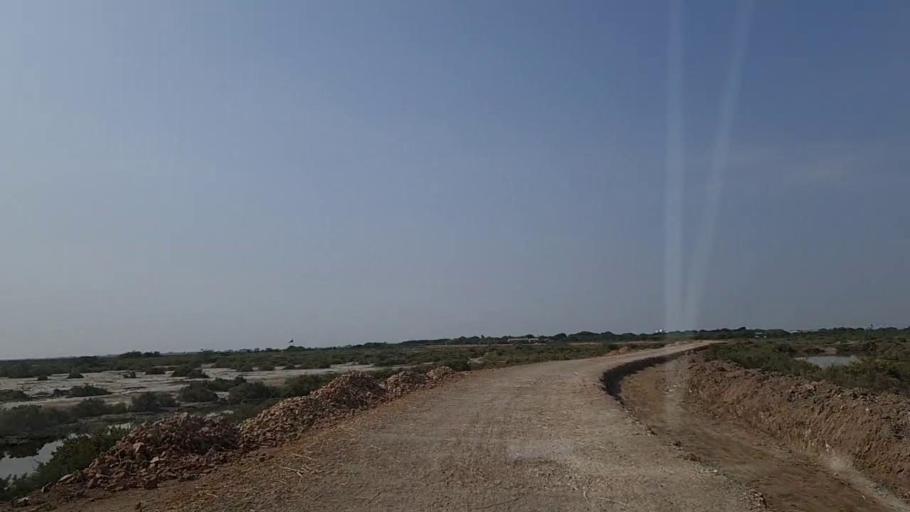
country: PK
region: Sindh
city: Chuhar Jamali
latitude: 24.1997
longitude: 67.8257
